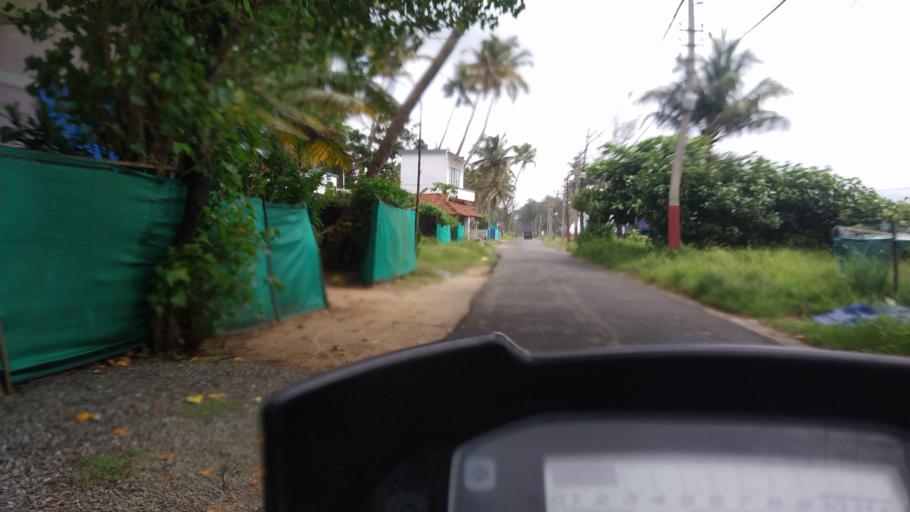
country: IN
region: Kerala
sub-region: Thrissur District
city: Kodungallur
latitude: 10.1563
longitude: 76.1734
